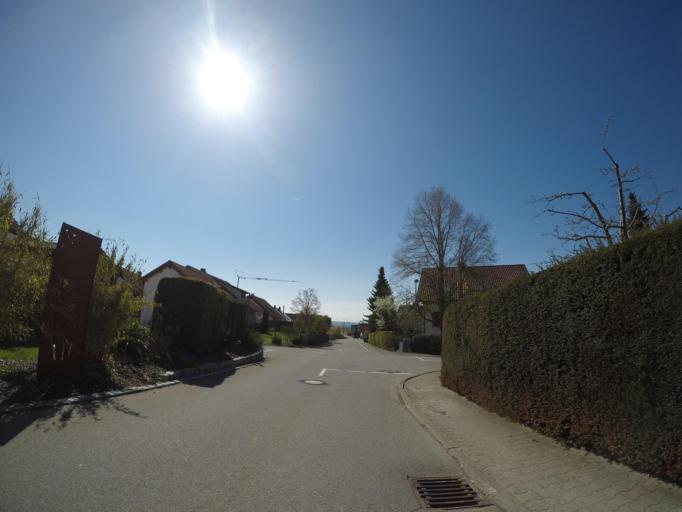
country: DE
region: Baden-Wuerttemberg
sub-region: Tuebingen Region
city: Wilhelmsdorf
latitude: 47.8635
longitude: 9.4292
